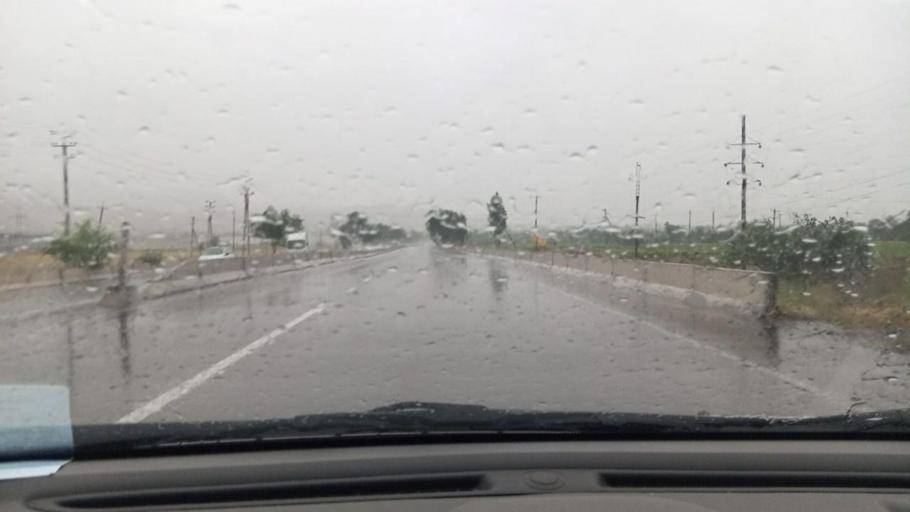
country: UZ
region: Toshkent
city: Ohangaron
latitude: 40.9185
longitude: 69.8341
